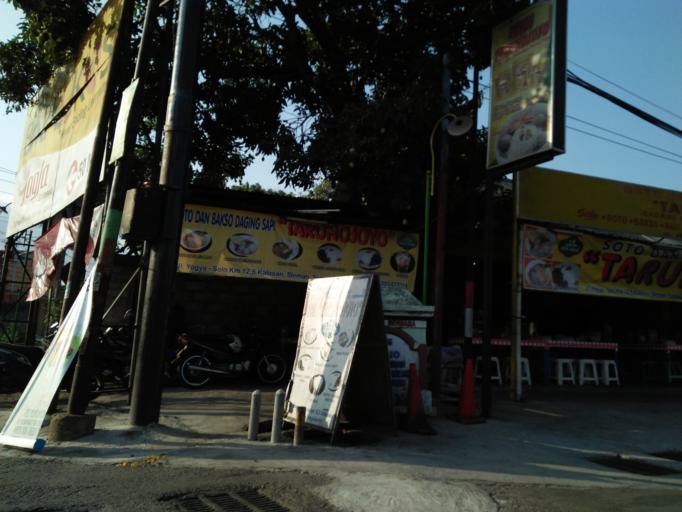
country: ID
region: Daerah Istimewa Yogyakarta
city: Depok
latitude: -7.7747
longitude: 110.4633
